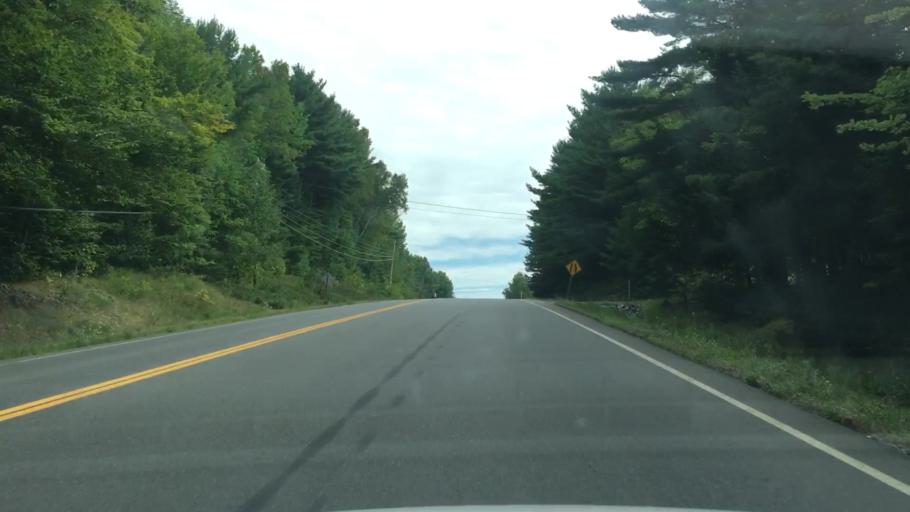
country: US
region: Maine
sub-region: Piscataquis County
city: Dover-Foxcroft
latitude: 45.2152
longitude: -69.1661
